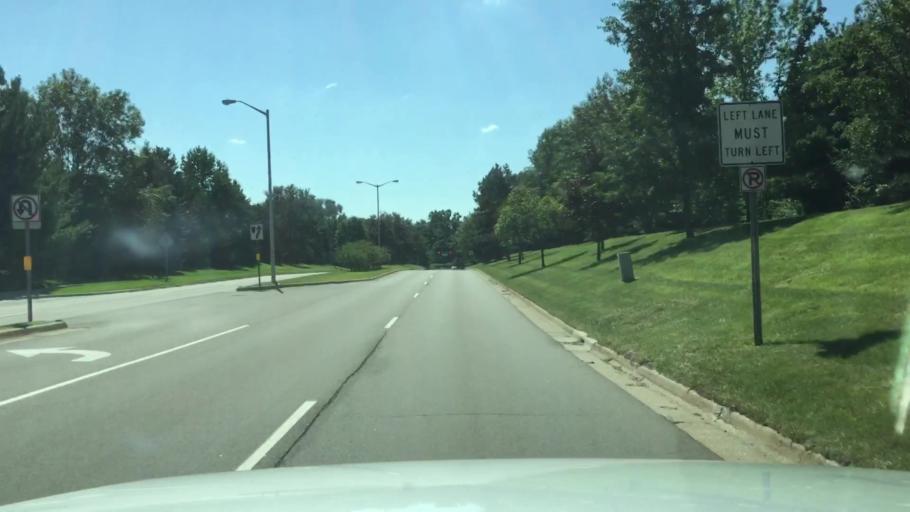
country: US
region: Michigan
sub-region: Kalamazoo County
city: Portage
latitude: 42.2183
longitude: -85.6033
